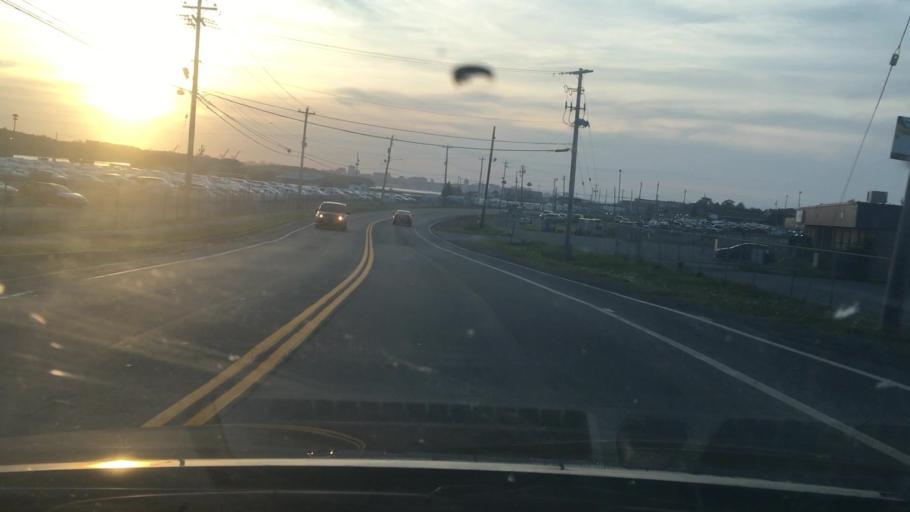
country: CA
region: Nova Scotia
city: Cole Harbour
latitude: 44.6201
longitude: -63.5048
